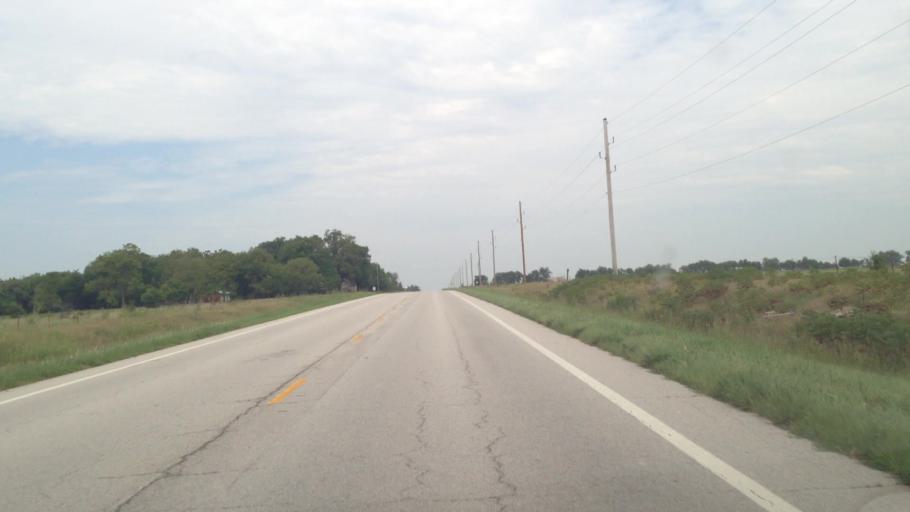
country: US
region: Kansas
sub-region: Allen County
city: Iola
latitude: 37.9667
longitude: -95.1701
